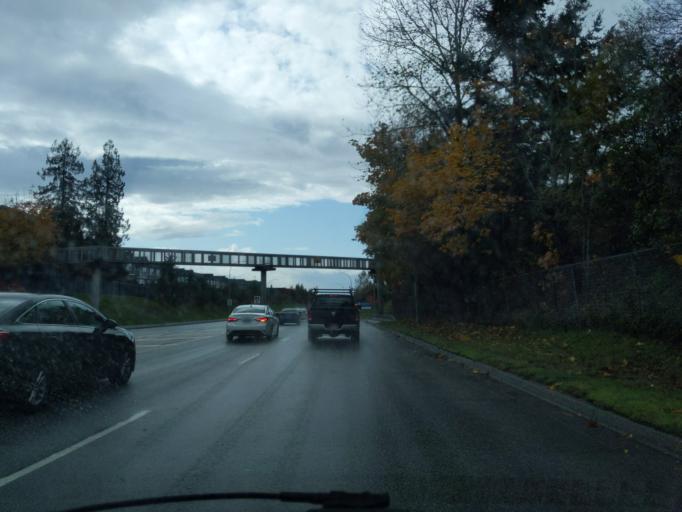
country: CA
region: British Columbia
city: Delta
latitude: 49.1564
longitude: -122.9295
